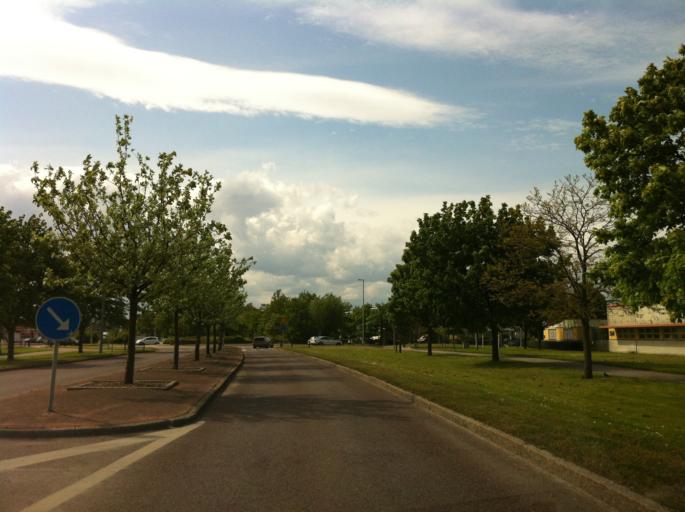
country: SE
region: Skane
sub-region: Landskrona
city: Landskrona
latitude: 55.8839
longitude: 12.8465
